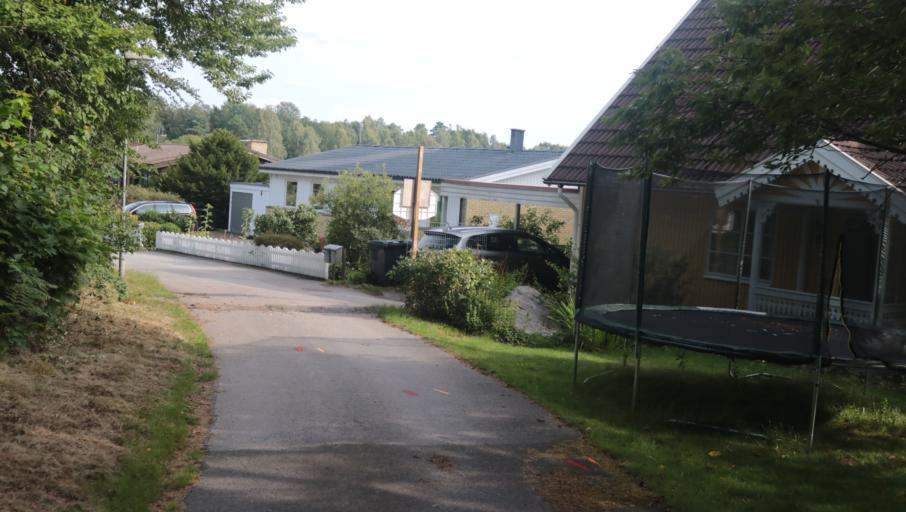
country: SE
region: Blekinge
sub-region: Karlshamns Kommun
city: Karlshamn
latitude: 56.2112
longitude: 14.8495
